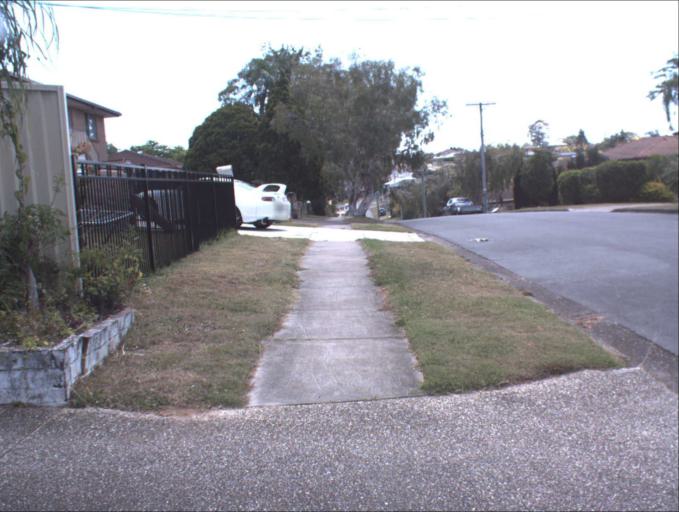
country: AU
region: Queensland
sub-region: Logan
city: Rochedale South
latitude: -27.5945
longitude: 153.1435
